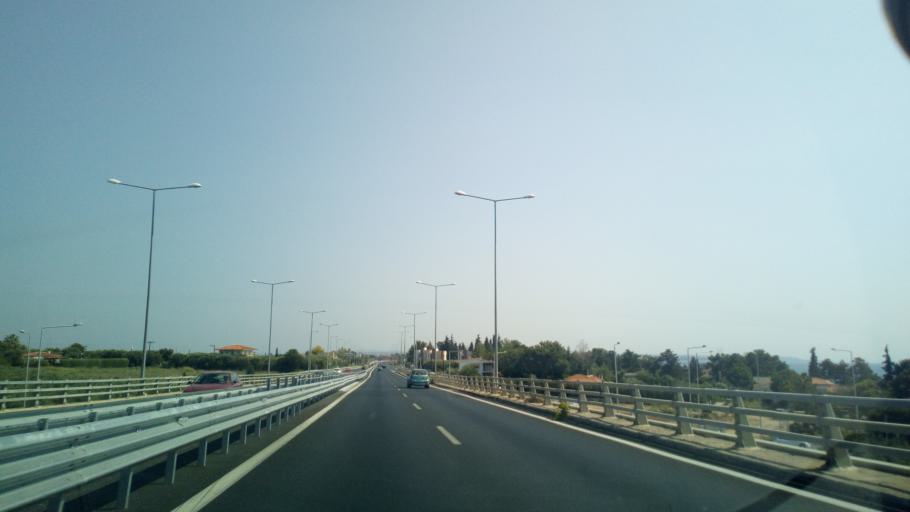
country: GR
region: Central Macedonia
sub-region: Nomos Chalkidikis
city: Nea Moudhania
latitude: 40.2256
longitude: 23.3134
